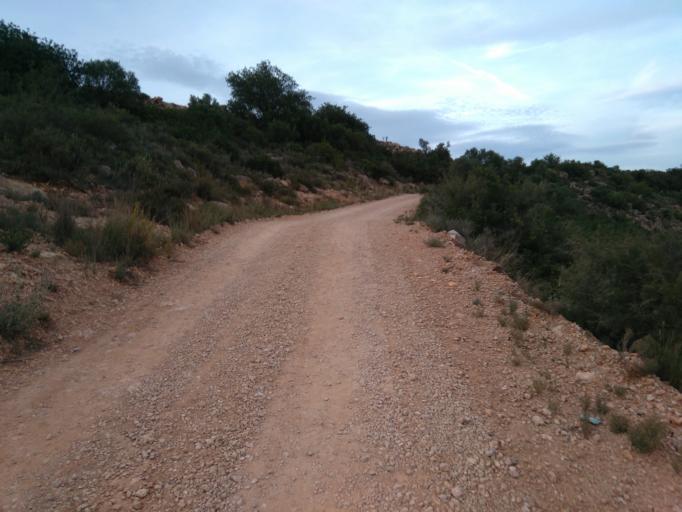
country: ES
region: Valencia
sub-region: Provincia de Valencia
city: Benimodo
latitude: 39.1989
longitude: -0.5857
